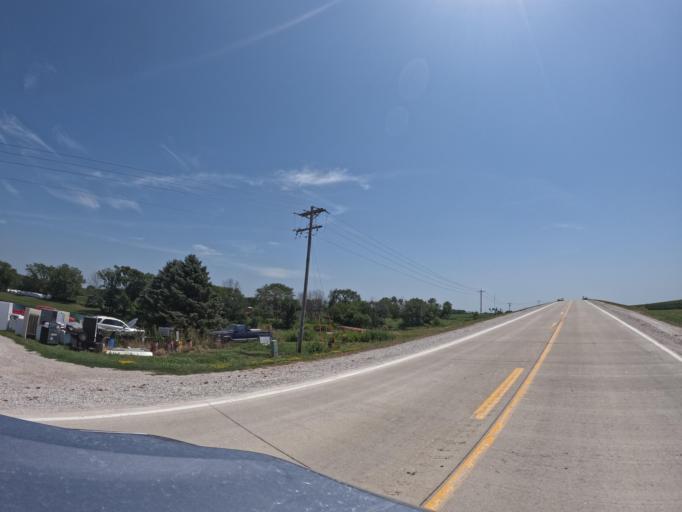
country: US
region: Iowa
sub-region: Henry County
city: Mount Pleasant
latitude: 40.9781
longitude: -91.6125
